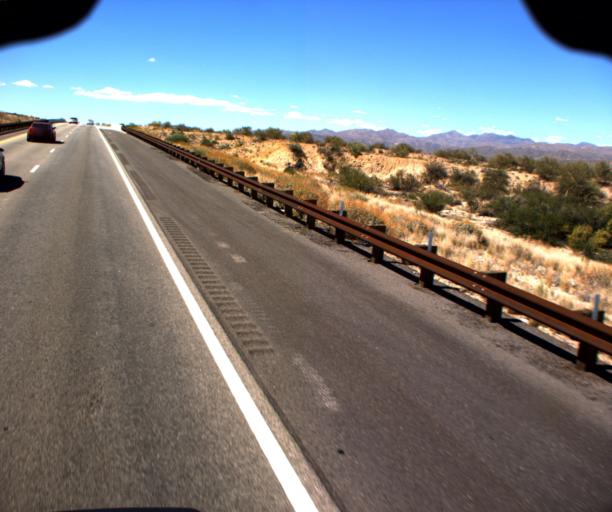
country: US
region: Arizona
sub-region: Mohave County
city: Kingman
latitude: 34.8607
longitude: -113.6411
